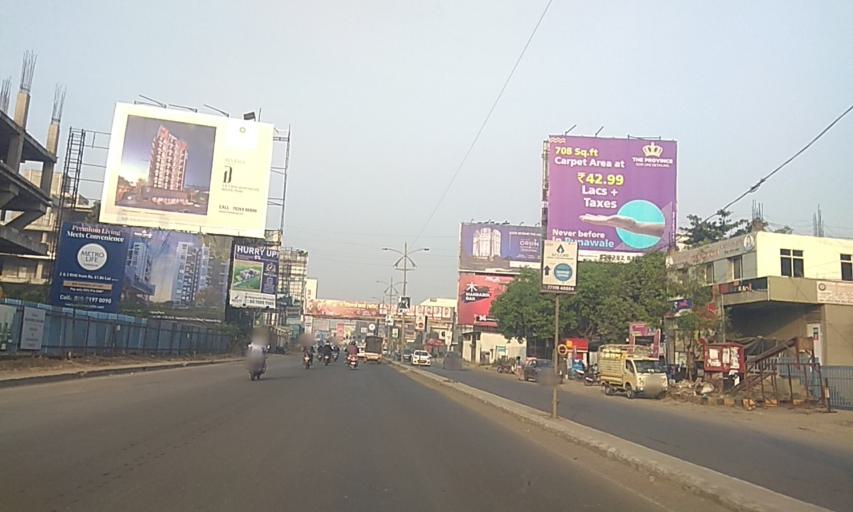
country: IN
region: Maharashtra
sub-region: Pune Division
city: Pimpri
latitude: 18.5908
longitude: 73.7467
